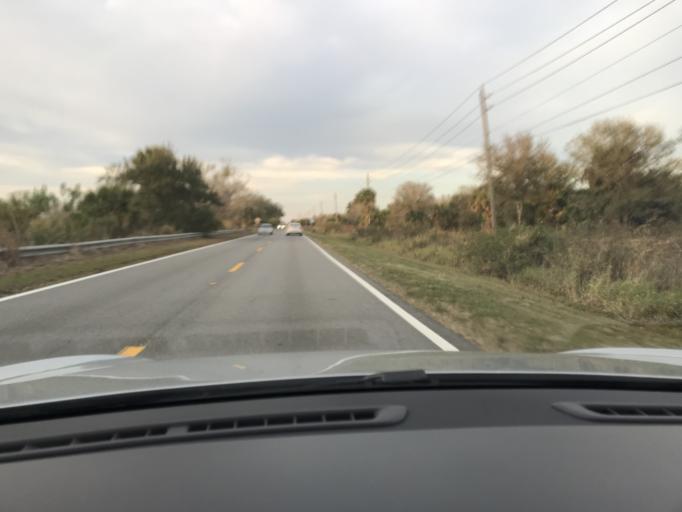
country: US
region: Florida
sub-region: Saint Lucie County
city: Lakewood Park
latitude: 27.5435
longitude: -80.4310
